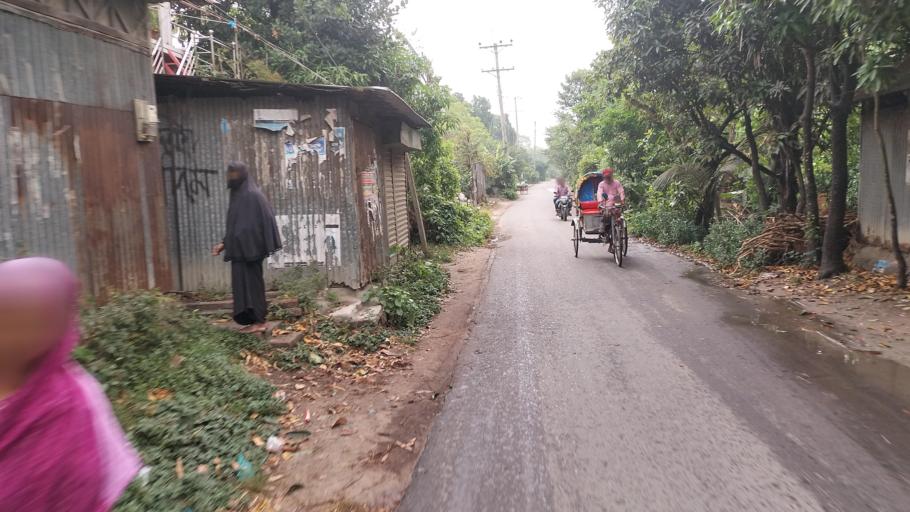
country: BD
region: Dhaka
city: Azimpur
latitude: 23.6758
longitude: 90.3470
